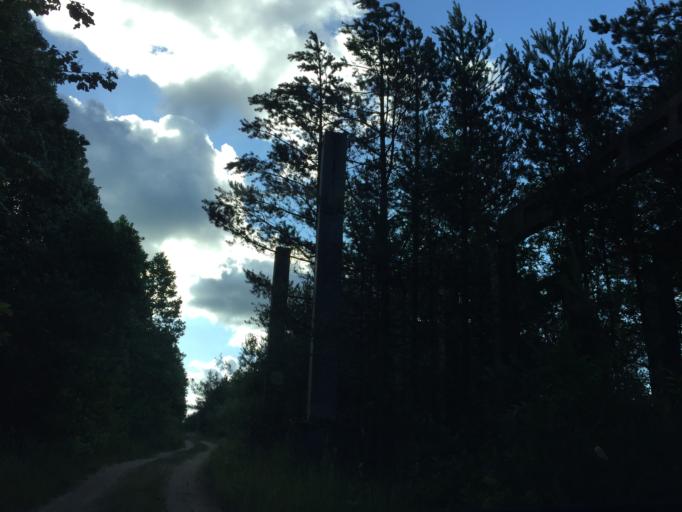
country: LV
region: Ventspils
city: Ventspils
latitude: 57.4099
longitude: 21.6227
